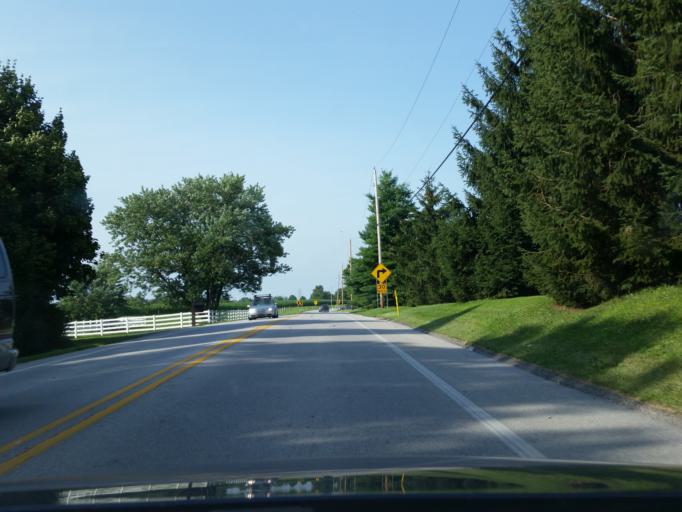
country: US
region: Pennsylvania
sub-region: York County
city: Shiloh
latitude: 39.9992
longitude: -76.7725
